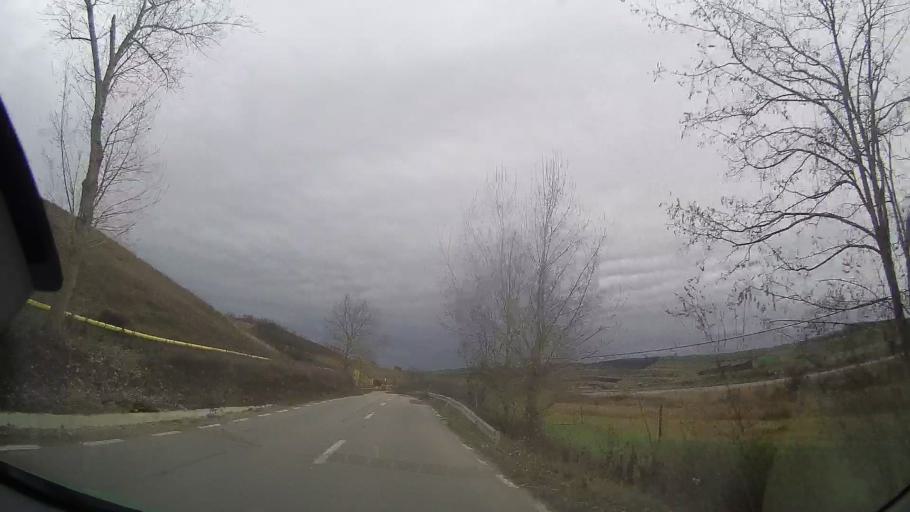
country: RO
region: Cluj
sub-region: Comuna Geaca
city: Geaca
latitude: 46.8441
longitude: 24.1368
